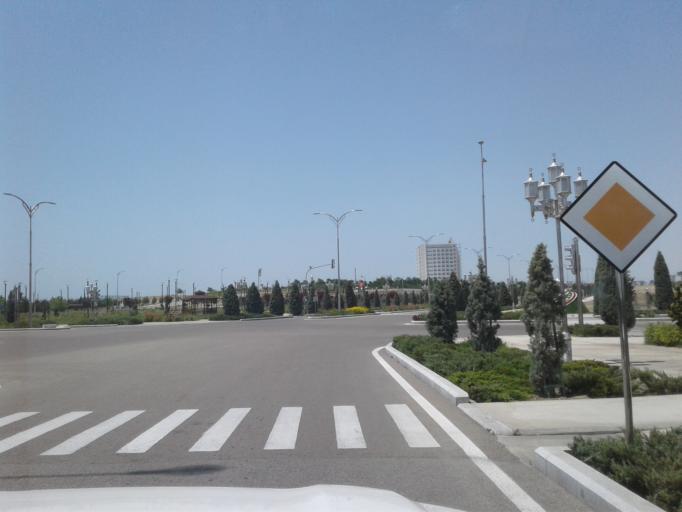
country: TM
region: Balkan
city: Turkmenbasy
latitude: 39.9520
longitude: 52.8558
